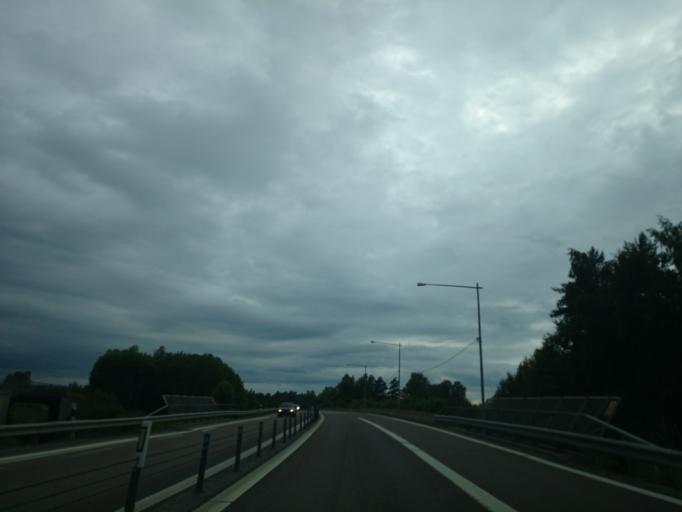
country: SE
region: Vaesternorrland
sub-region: Timra Kommun
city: Bergeforsen
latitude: 62.5163
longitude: 17.3883
